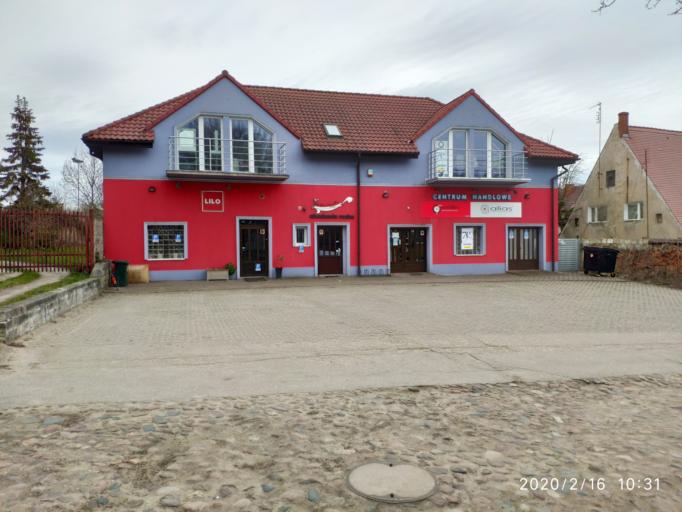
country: PL
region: Lubusz
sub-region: Zielona Gora
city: Zielona Gora
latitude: 51.9357
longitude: 15.5093
